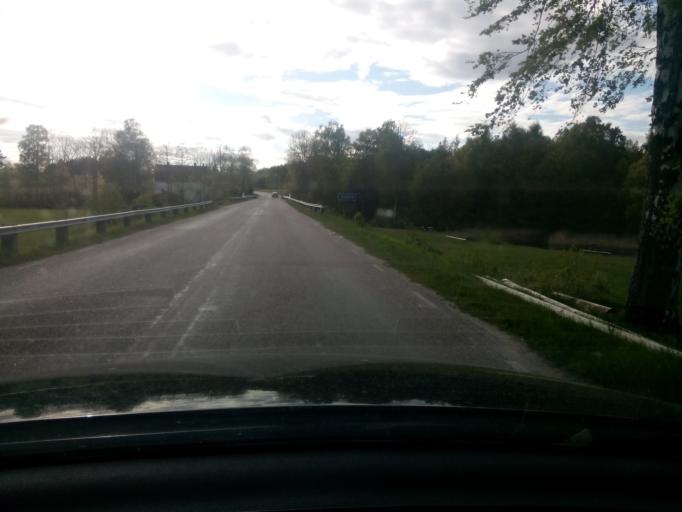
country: SE
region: Soedermanland
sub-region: Nykopings Kommun
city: Stigtomta
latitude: 58.9506
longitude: 16.8843
